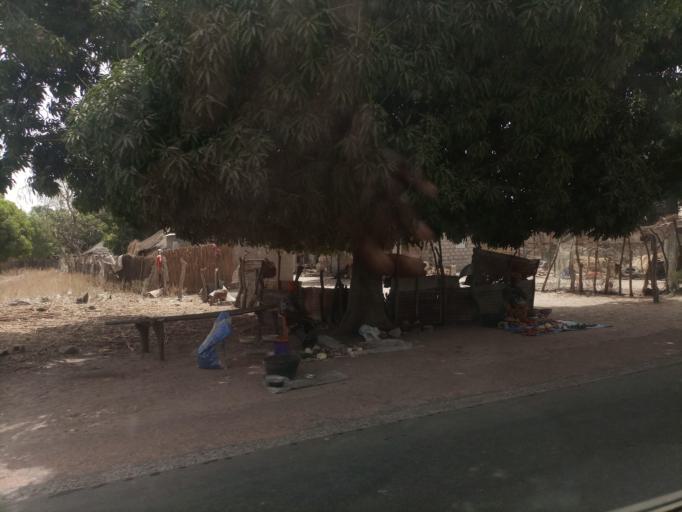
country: SN
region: Fatick
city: Sokone
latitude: 13.7130
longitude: -16.4266
